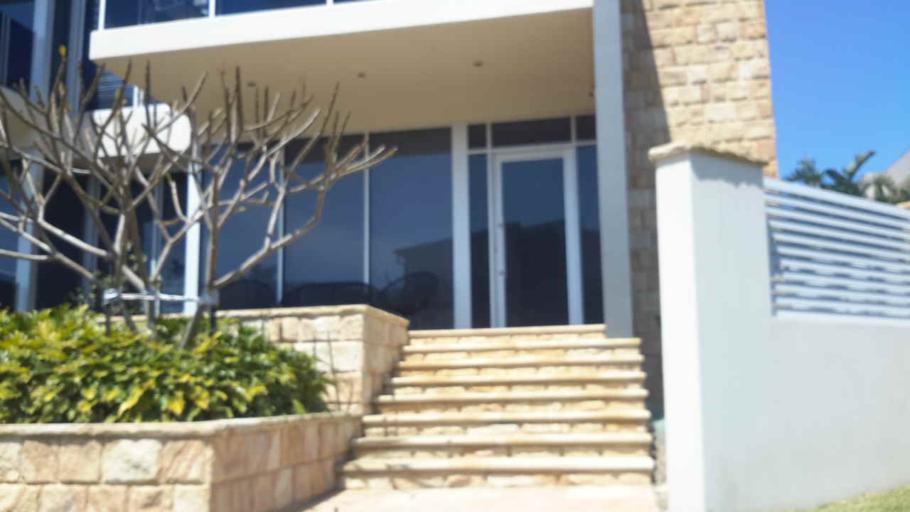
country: AU
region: New South Wales
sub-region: Wollongong
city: Bulli
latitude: -34.3285
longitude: 150.9234
